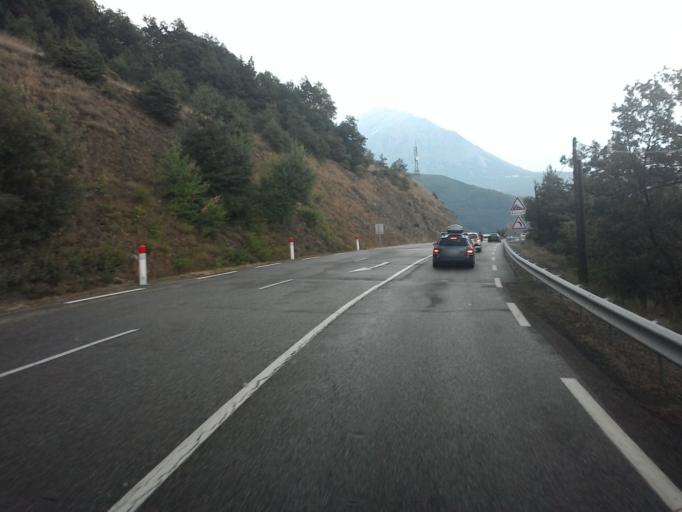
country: FR
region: Provence-Alpes-Cote d'Azur
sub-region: Departement des Hautes-Alpes
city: Saint-Bonnet-en-Champsaur
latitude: 44.8029
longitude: 5.9615
